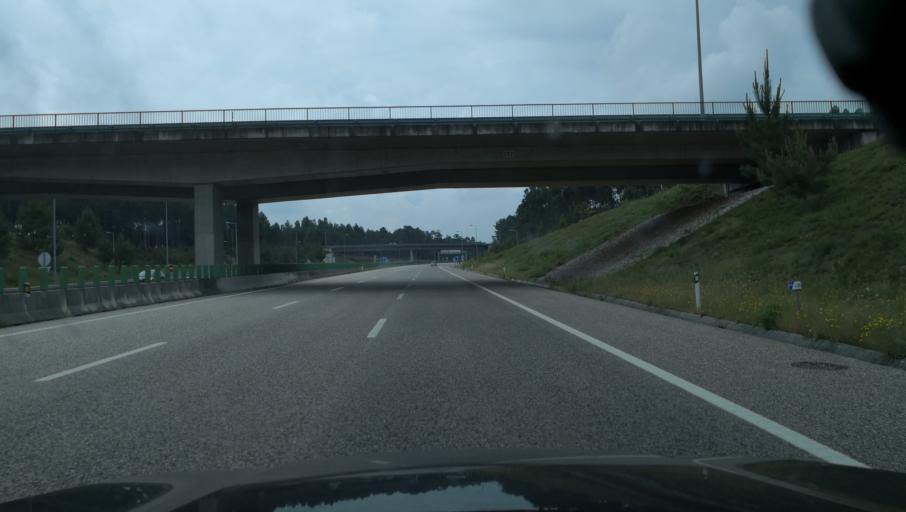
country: PT
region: Leiria
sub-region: Pombal
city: Lourical
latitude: 39.9446
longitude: -8.7705
